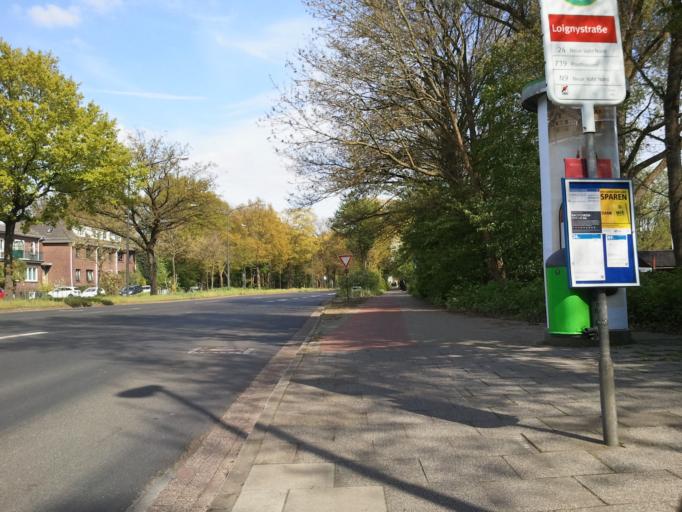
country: DE
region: Bremen
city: Bremen
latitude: 53.0824
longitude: 8.8600
